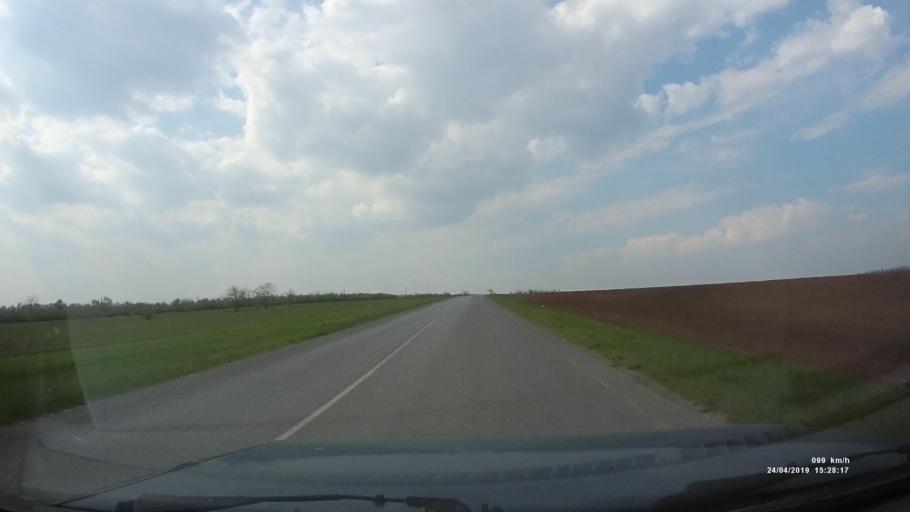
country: RU
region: Rostov
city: Remontnoye
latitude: 46.5766
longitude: 43.0194
